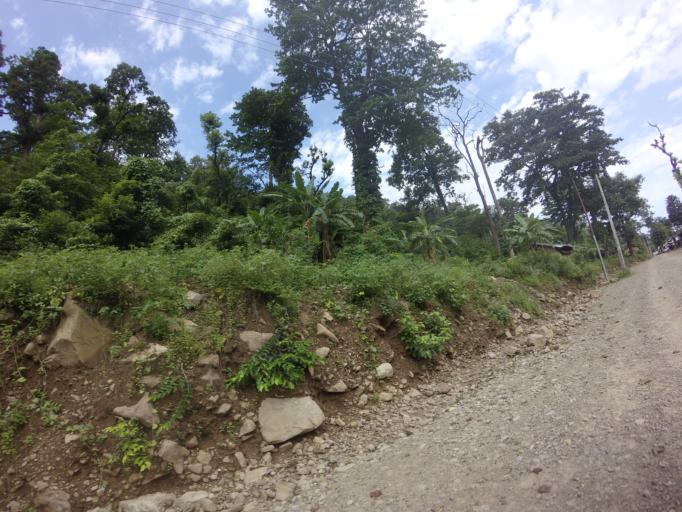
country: NP
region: Far Western
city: Tikapur
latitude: 28.6570
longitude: 81.2864
